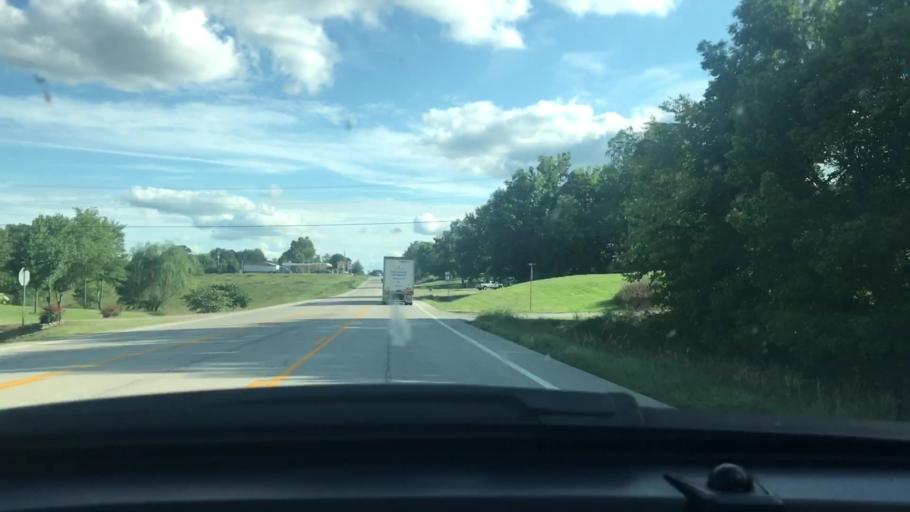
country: US
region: Missouri
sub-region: Oregon County
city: Thayer
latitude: 36.5985
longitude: -91.6440
